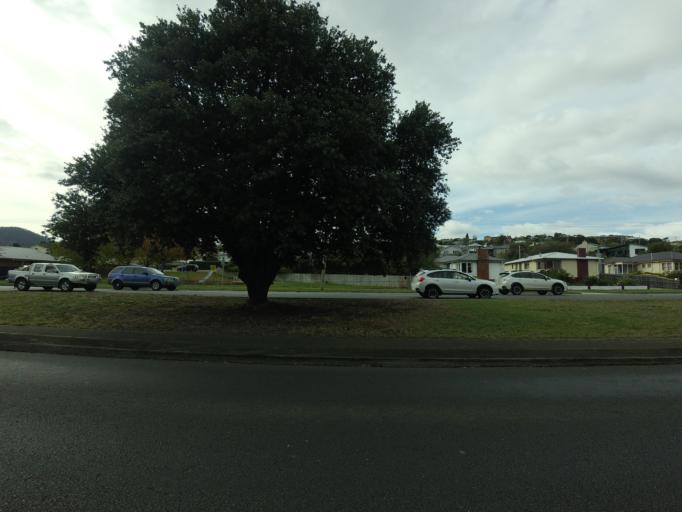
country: AU
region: Tasmania
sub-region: Glenorchy
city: Moonah
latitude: -42.8398
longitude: 147.3045
